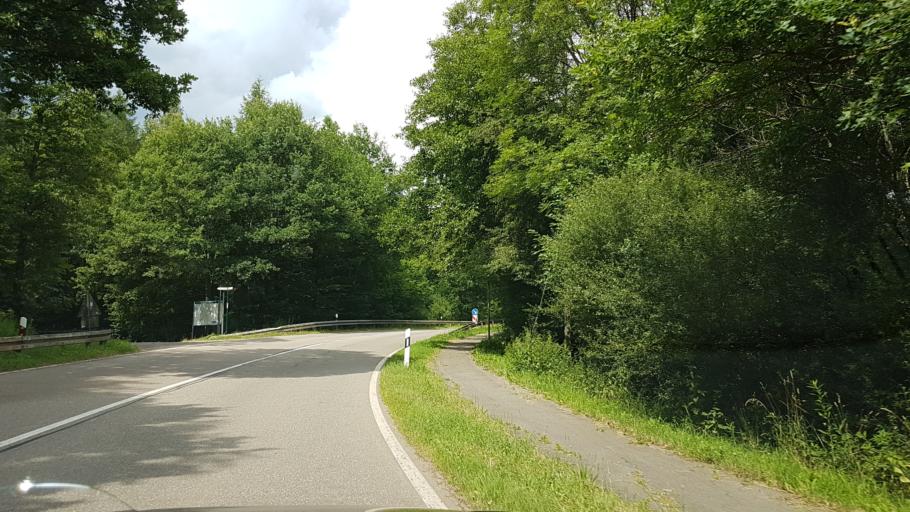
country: DE
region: Saarland
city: Saarbrucken
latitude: 49.2672
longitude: 6.9842
